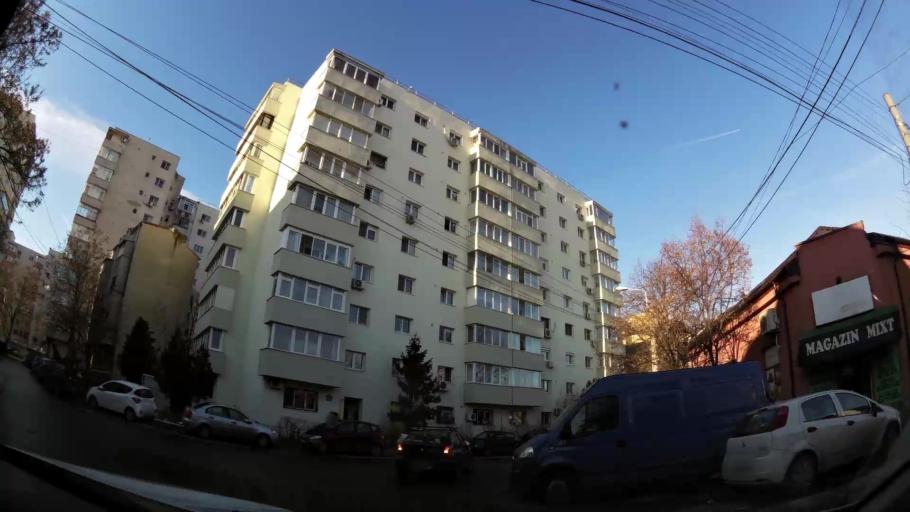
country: RO
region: Bucuresti
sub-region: Municipiul Bucuresti
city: Bucharest
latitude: 44.4443
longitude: 26.1215
